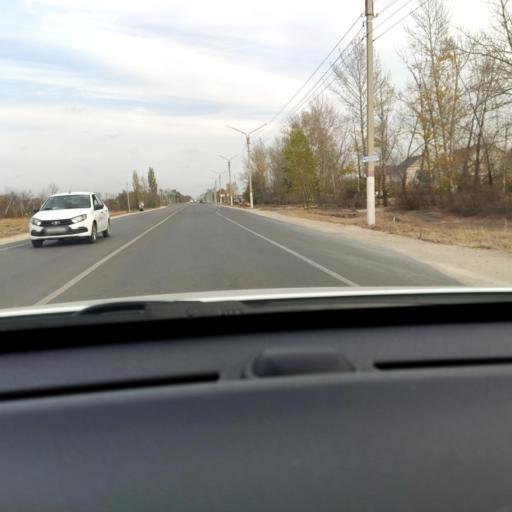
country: RU
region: Voronezj
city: Novaya Usman'
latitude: 51.6561
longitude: 39.4333
